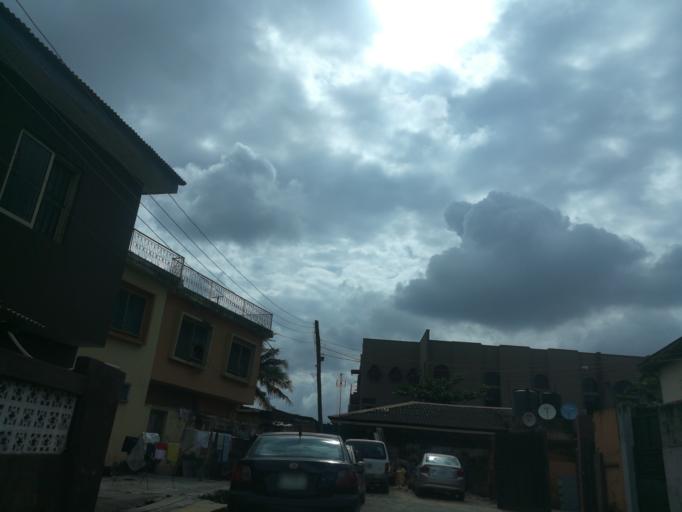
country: NG
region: Lagos
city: Agege
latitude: 6.6247
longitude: 3.3335
